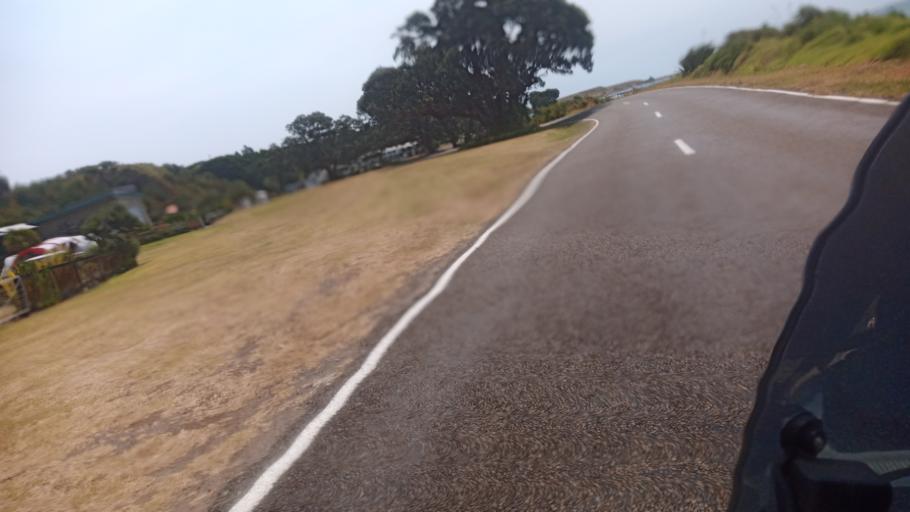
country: NZ
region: Bay of Plenty
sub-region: Opotiki District
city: Opotiki
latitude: -37.6178
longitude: 177.9106
